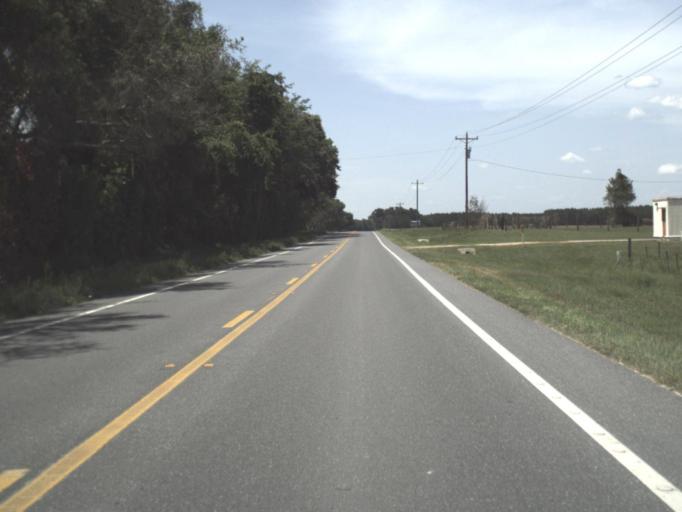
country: US
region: Florida
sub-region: Gilchrist County
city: Trenton
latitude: 29.8224
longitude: -82.8672
